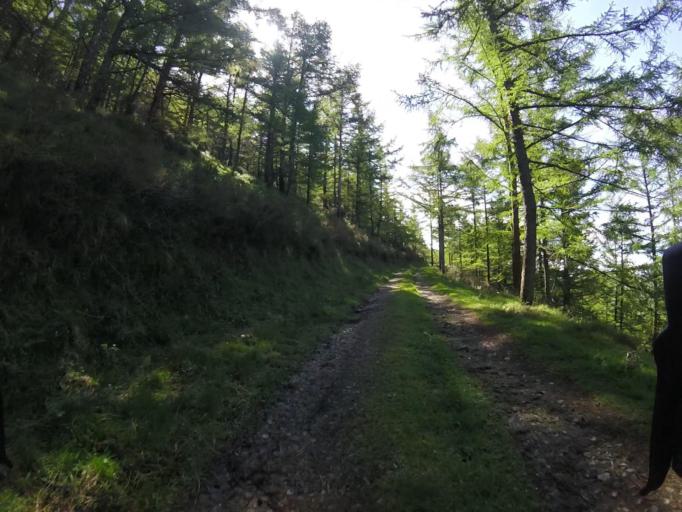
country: ES
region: Navarre
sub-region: Provincia de Navarra
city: Arano
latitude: 43.1824
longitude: -1.9502
